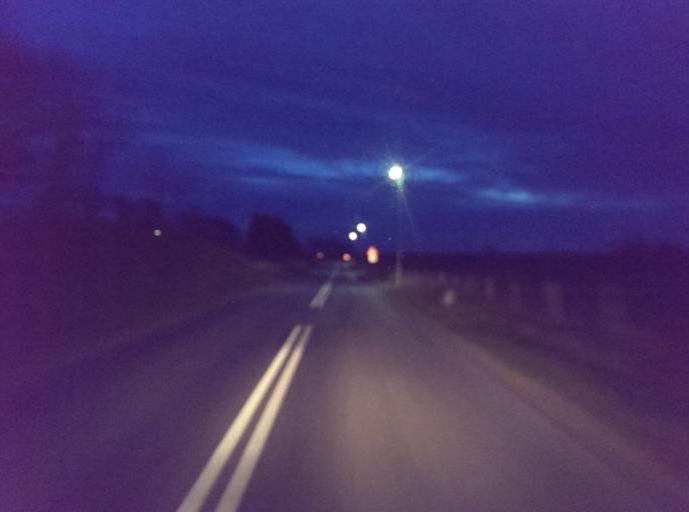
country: DK
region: South Denmark
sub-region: Esbjerg Kommune
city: Tjaereborg
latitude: 55.4731
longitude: 8.5313
